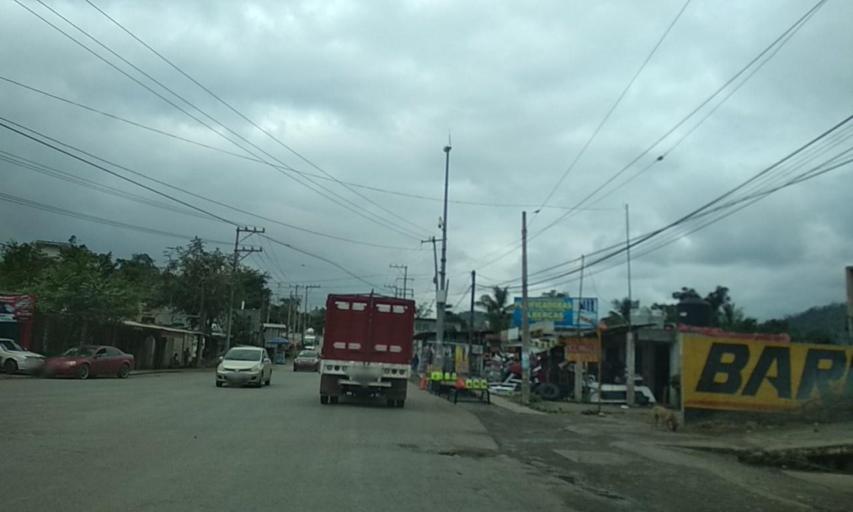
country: MX
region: Veracruz
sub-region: Papantla
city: El Chote
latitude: 20.3997
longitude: -97.3358
